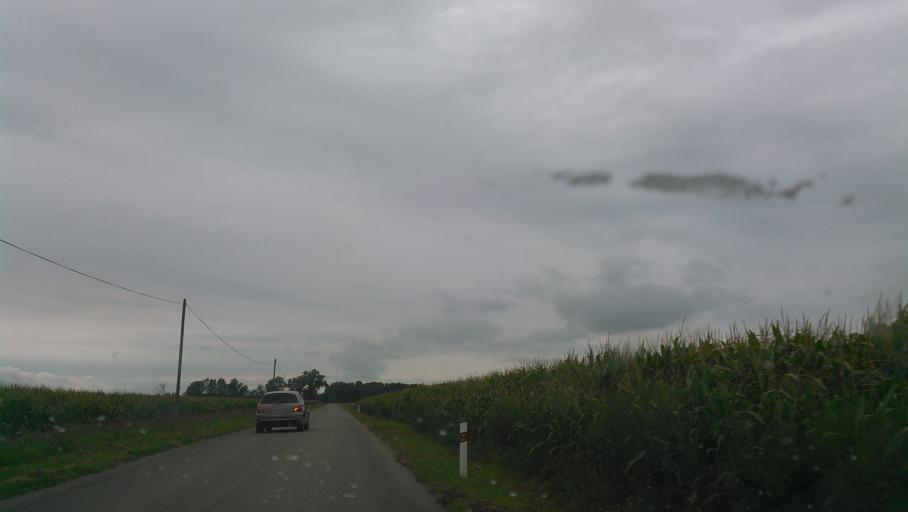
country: SK
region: Nitriansky
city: Kolarovo
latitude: 47.8788
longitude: 17.9118
